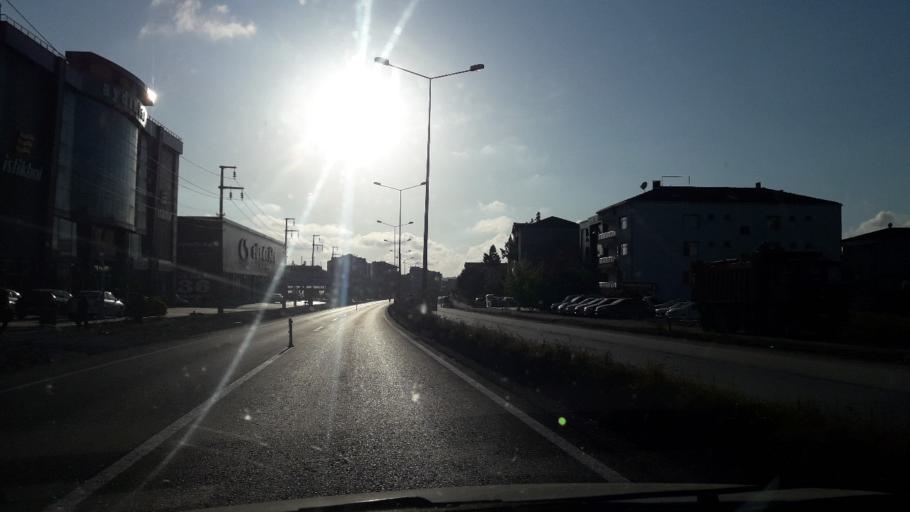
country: TR
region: Samsun
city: Bafra
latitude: 41.5579
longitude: 35.9025
